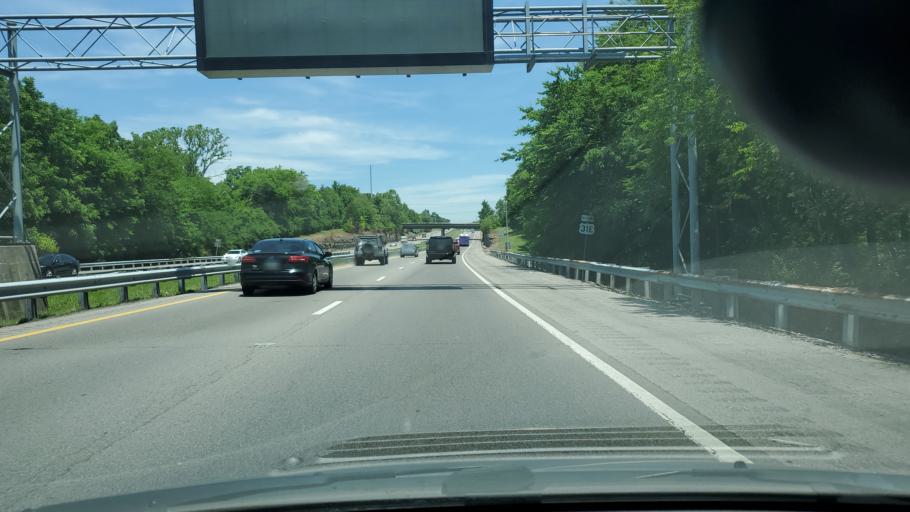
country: US
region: Tennessee
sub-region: Davidson County
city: Nashville
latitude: 36.1971
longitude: -86.7521
